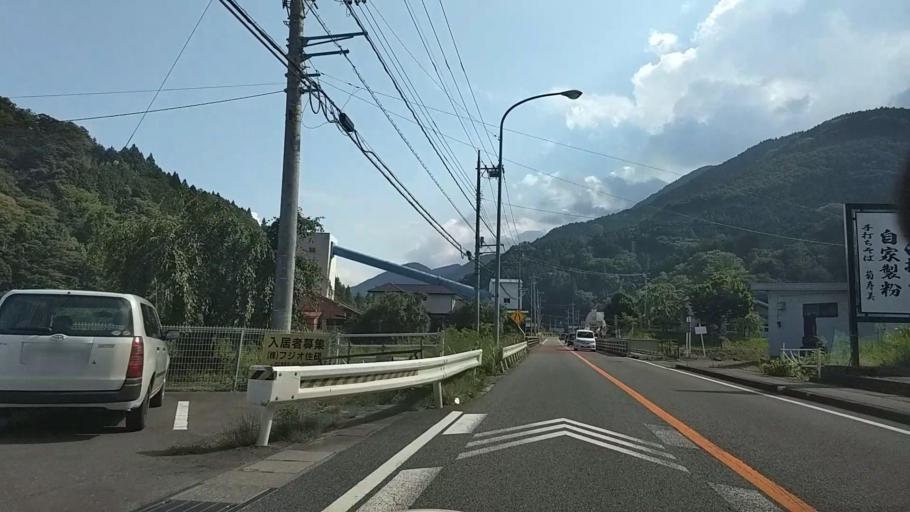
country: JP
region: Shizuoka
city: Fujinomiya
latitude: 35.3541
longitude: 138.4221
